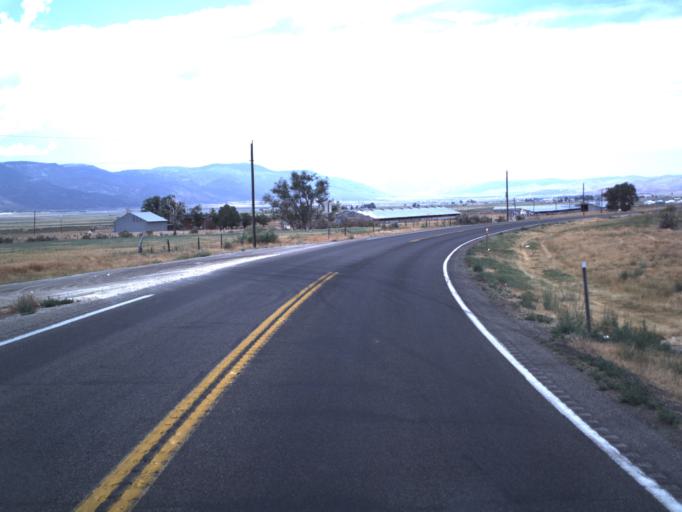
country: US
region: Utah
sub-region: Sanpete County
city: Ephraim
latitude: 39.4235
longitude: -111.5618
